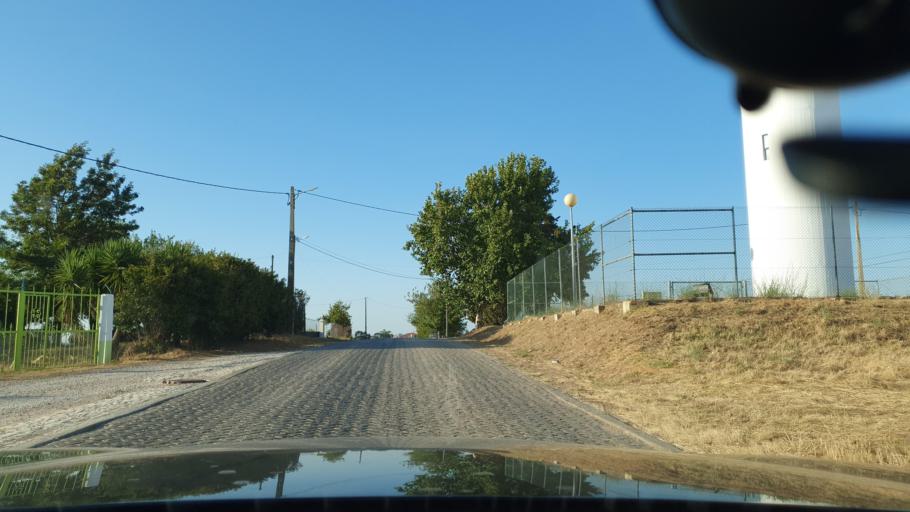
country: PT
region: Portalegre
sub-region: Fronteira
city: Fronteira
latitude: 38.9434
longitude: -7.6773
